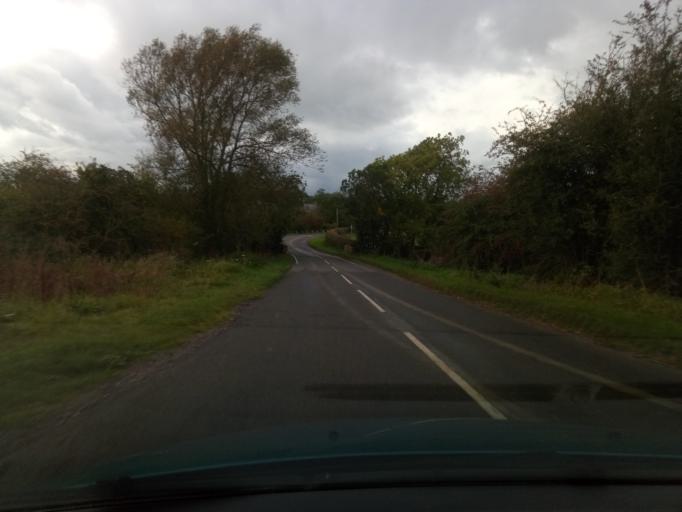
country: GB
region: England
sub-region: Leicestershire
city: Sileby
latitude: 52.7498
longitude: -1.0784
